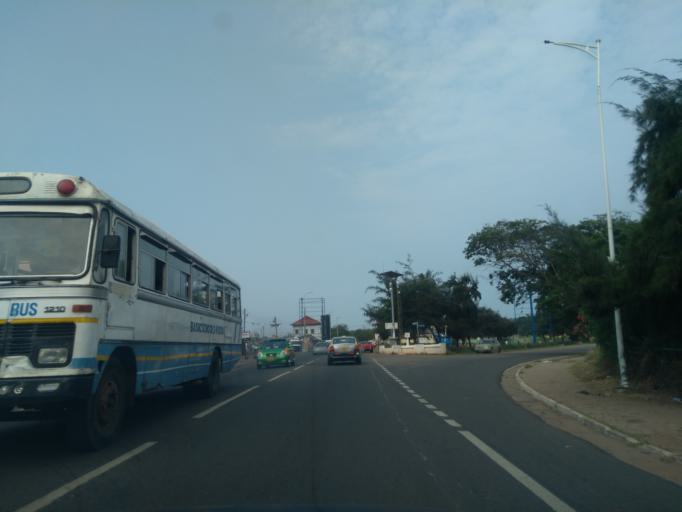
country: GH
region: Greater Accra
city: Accra
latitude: 5.5494
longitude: -0.1906
